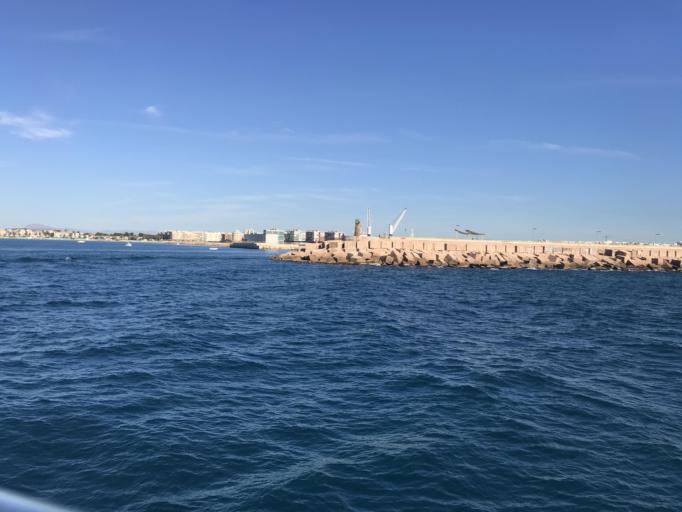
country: ES
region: Valencia
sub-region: Provincia de Alicante
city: Torrevieja
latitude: 37.9629
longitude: -0.6868
